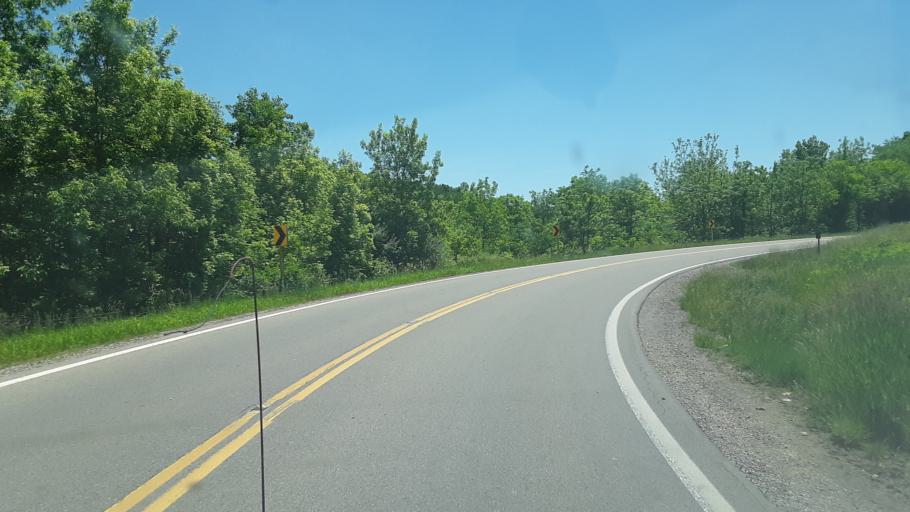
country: US
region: Ohio
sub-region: Coshocton County
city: Coshocton
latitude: 40.3068
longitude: -82.0110
